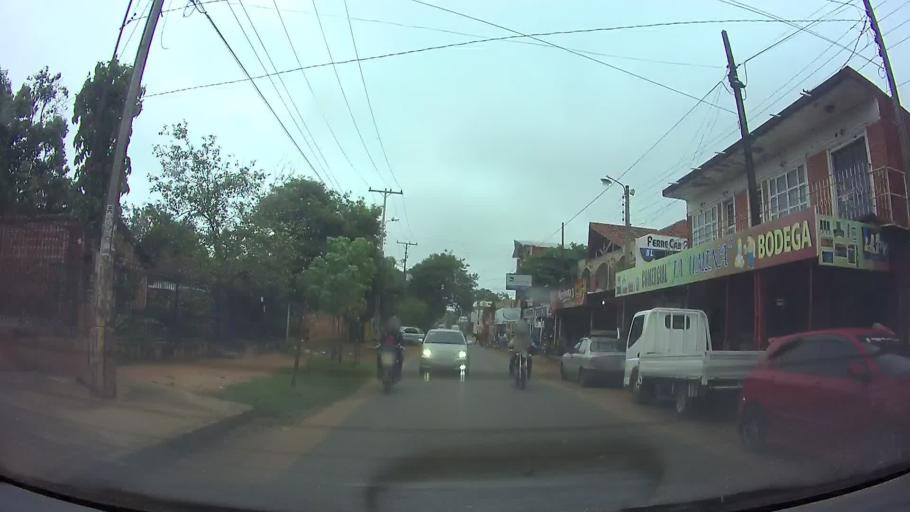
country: PY
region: Central
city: San Lorenzo
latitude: -25.3248
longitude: -57.5008
